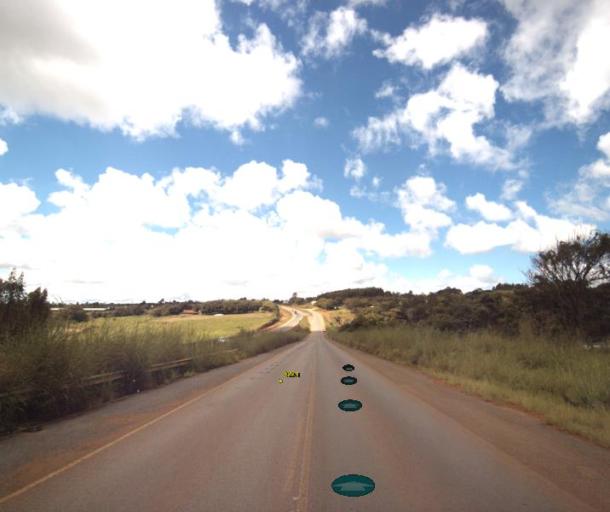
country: BR
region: Goias
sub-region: Anapolis
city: Anapolis
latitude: -16.2418
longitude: -49.0034
